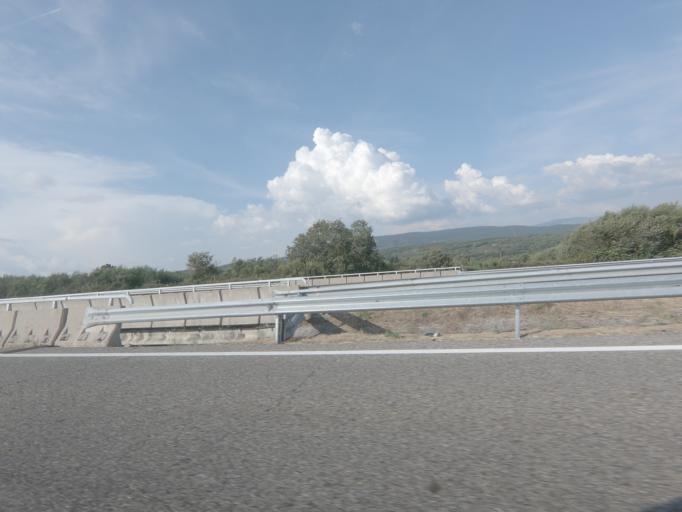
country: ES
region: Galicia
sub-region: Provincia de Ourense
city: Cualedro
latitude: 41.9843
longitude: -7.5478
